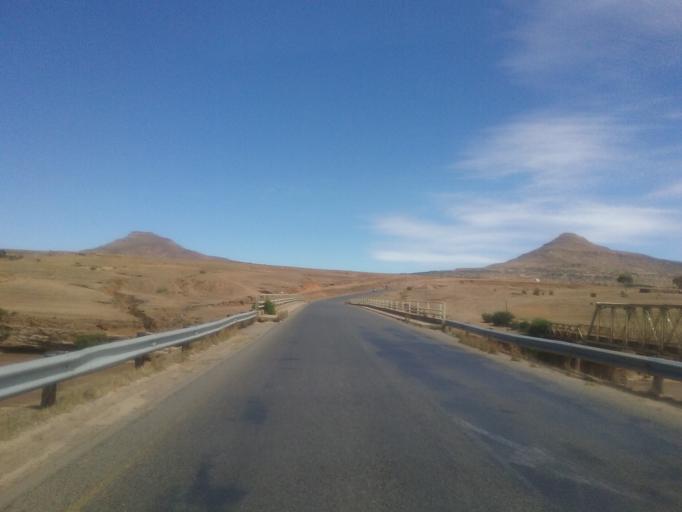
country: LS
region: Mohale's Hoek District
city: Mohale's Hoek
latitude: -30.0903
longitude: 27.4344
